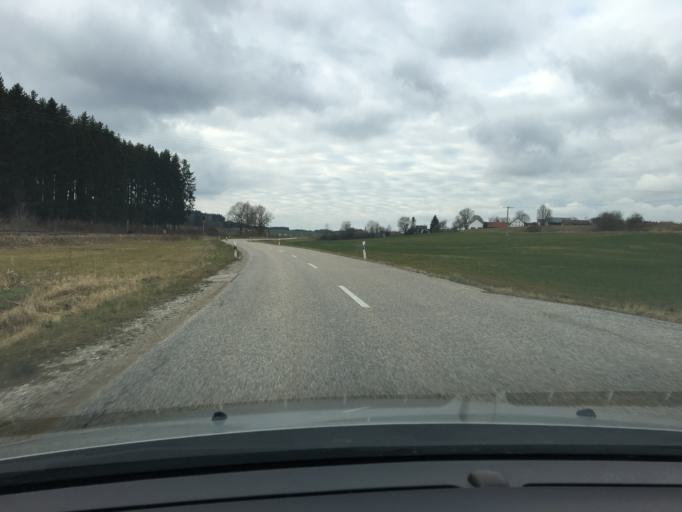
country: DE
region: Bavaria
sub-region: Lower Bavaria
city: Geisenhausen
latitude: 48.4829
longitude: 12.2318
